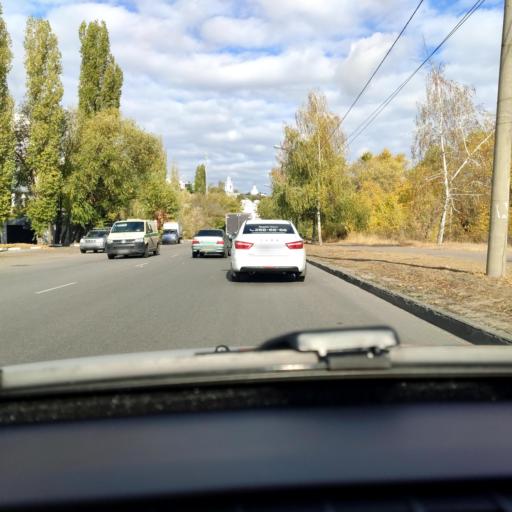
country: RU
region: Voronezj
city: Voronezh
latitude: 51.6538
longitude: 39.2121
